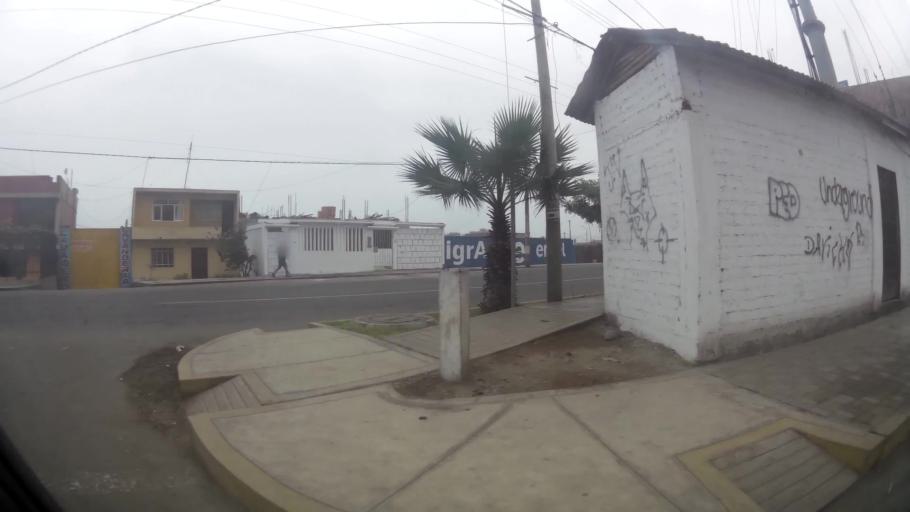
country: PE
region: Lima
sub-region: Provincia de Huaral
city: Chancay
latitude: -11.5741
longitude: -77.2695
